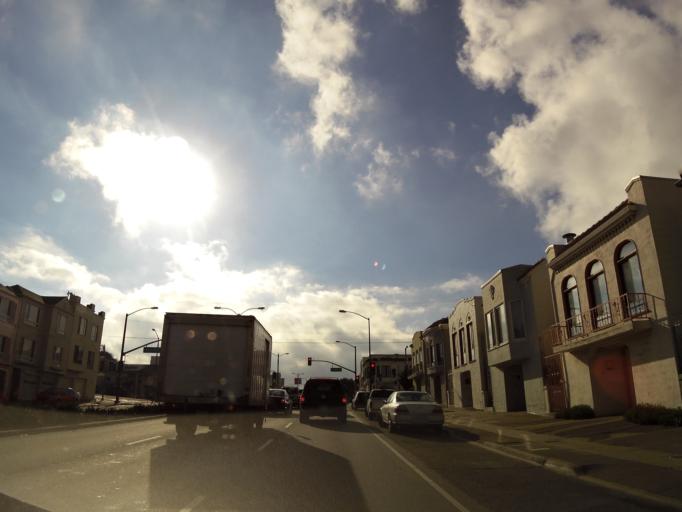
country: US
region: California
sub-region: San Mateo County
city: Daly City
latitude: 37.7511
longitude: -122.4763
